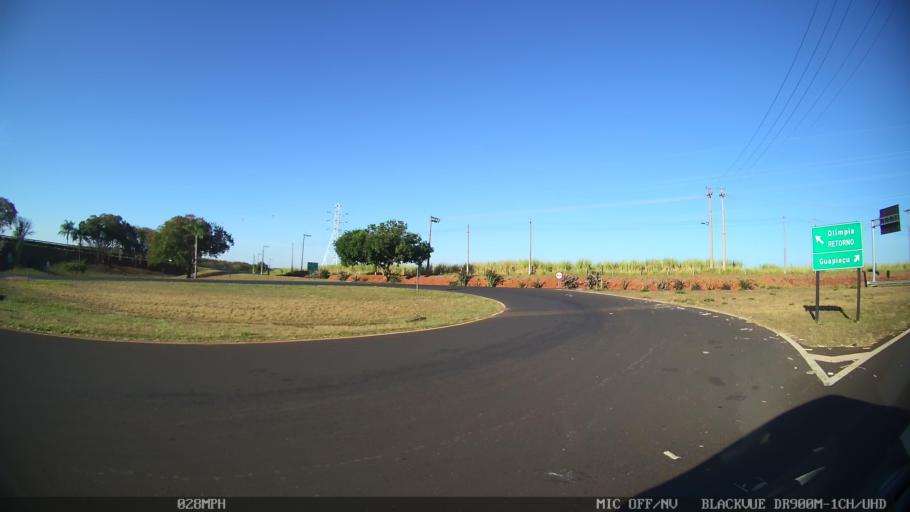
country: BR
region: Sao Paulo
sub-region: Guapiacu
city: Guapiacu
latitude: -20.7746
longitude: -49.2252
